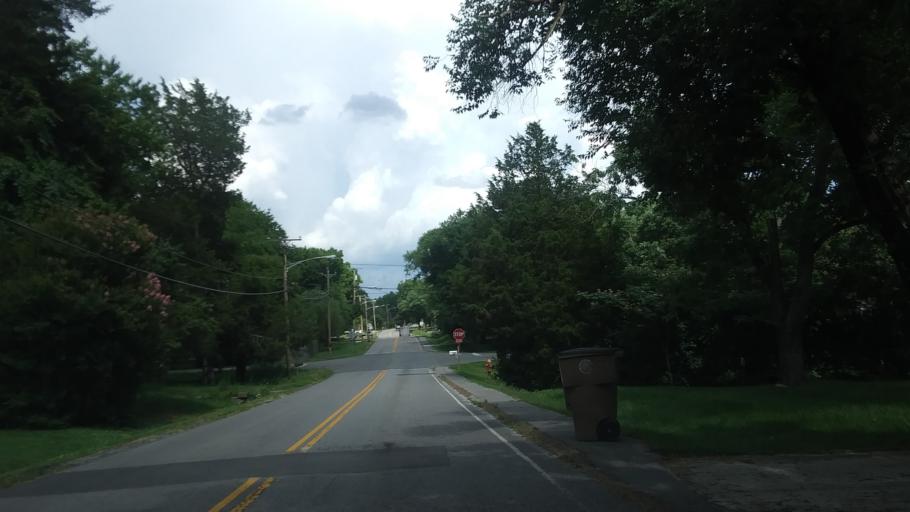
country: US
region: Tennessee
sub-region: Davidson County
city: Oak Hill
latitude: 36.0637
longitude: -86.7118
